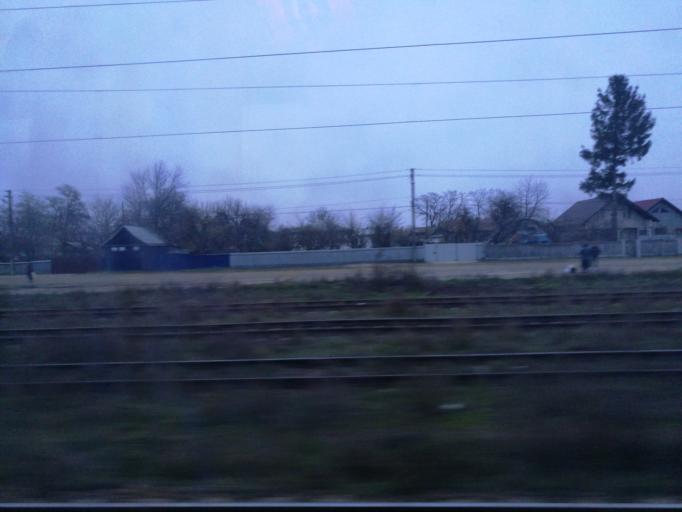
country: RO
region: Suceava
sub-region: Comuna Veresti
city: Veresti
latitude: 47.6085
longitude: 26.4374
